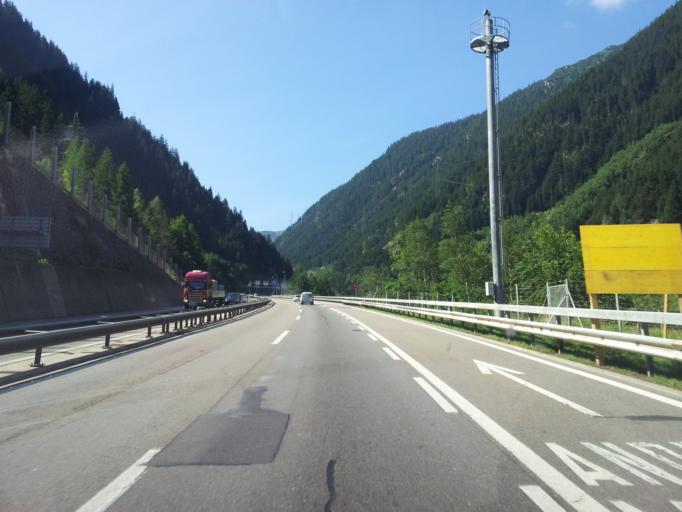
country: CH
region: Uri
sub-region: Uri
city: Andermatt
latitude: 46.6927
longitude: 8.5957
